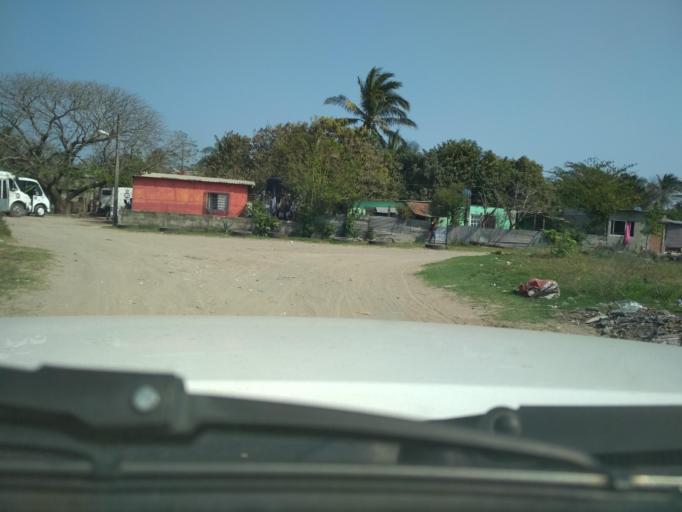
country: MX
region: Veracruz
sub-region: Veracruz
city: Rio Medio [Granja]
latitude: 19.2119
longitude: -96.2104
